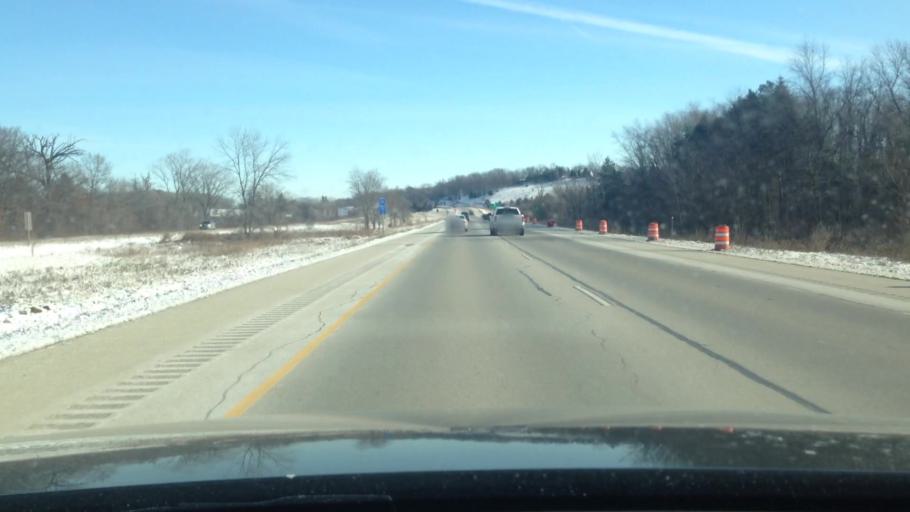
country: US
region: Wisconsin
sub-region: Waukesha County
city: Muskego
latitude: 42.9387
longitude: -88.1398
